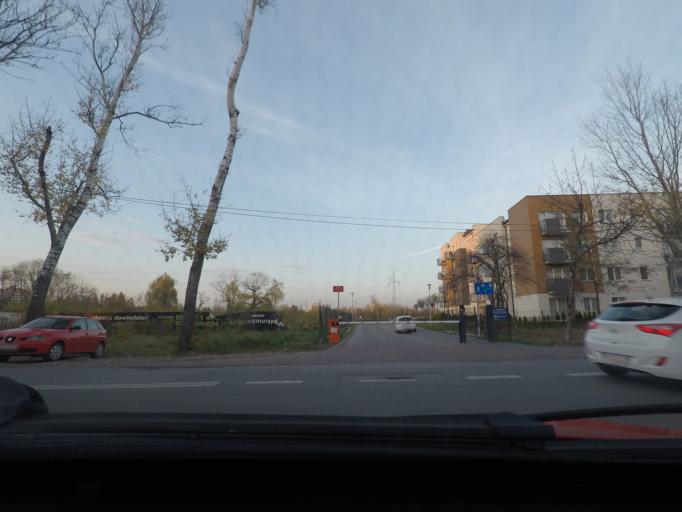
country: PL
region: Lesser Poland Voivodeship
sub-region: Krakow
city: Krakow
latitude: 50.0357
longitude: 19.9317
